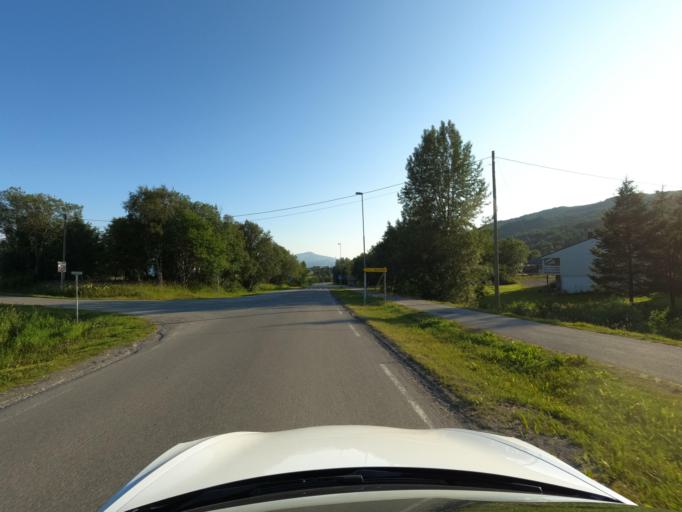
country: NO
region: Nordland
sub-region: Evenes
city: Randa
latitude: 68.4831
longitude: 16.8930
